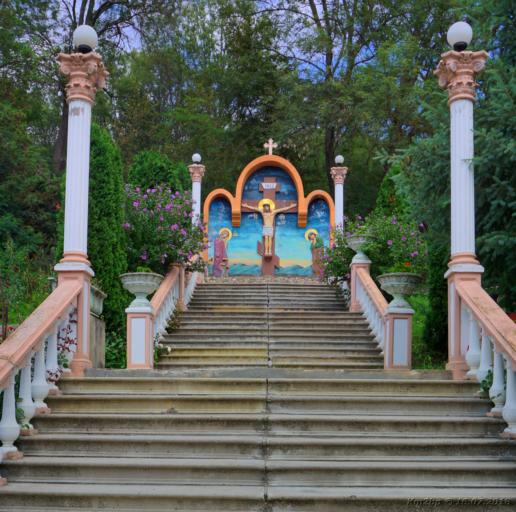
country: MD
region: Stinga Nistrului
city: Bucovat
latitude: 47.3155
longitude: 28.5128
